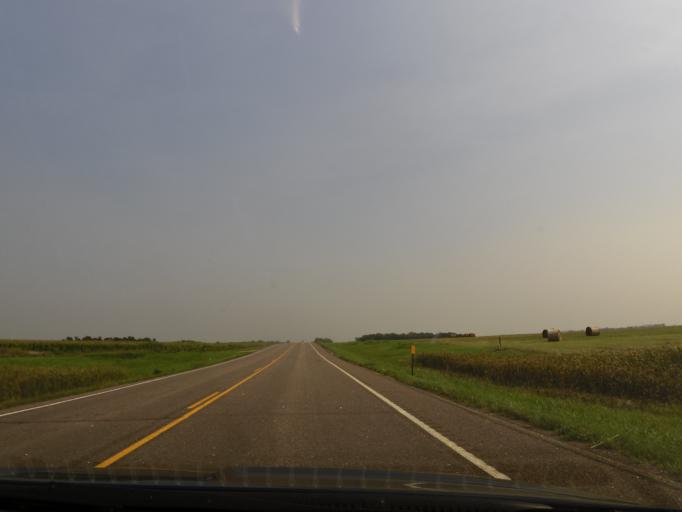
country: US
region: South Dakota
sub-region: Roberts County
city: Sisseton
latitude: 45.8486
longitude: -96.9754
